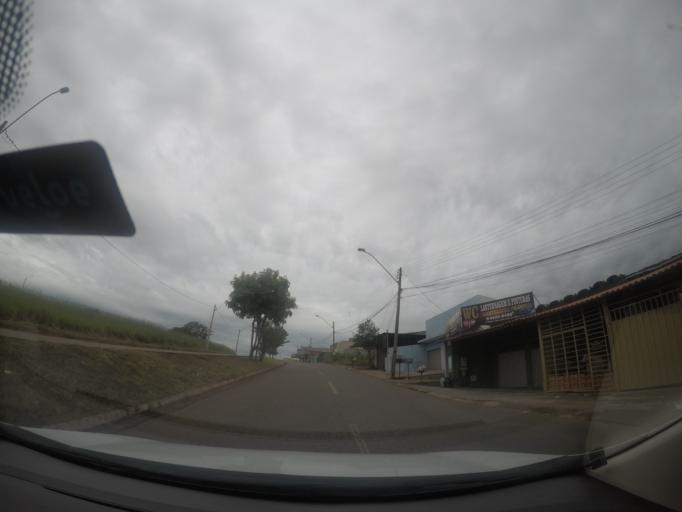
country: BR
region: Goias
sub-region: Goiania
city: Goiania
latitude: -16.6176
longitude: -49.3055
